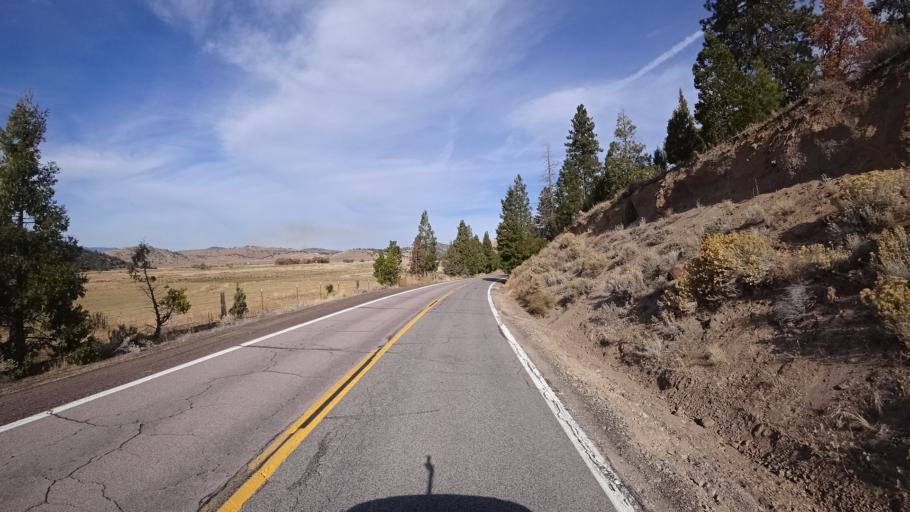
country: US
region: California
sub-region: Siskiyou County
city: Weed
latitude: 41.4794
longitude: -122.4111
